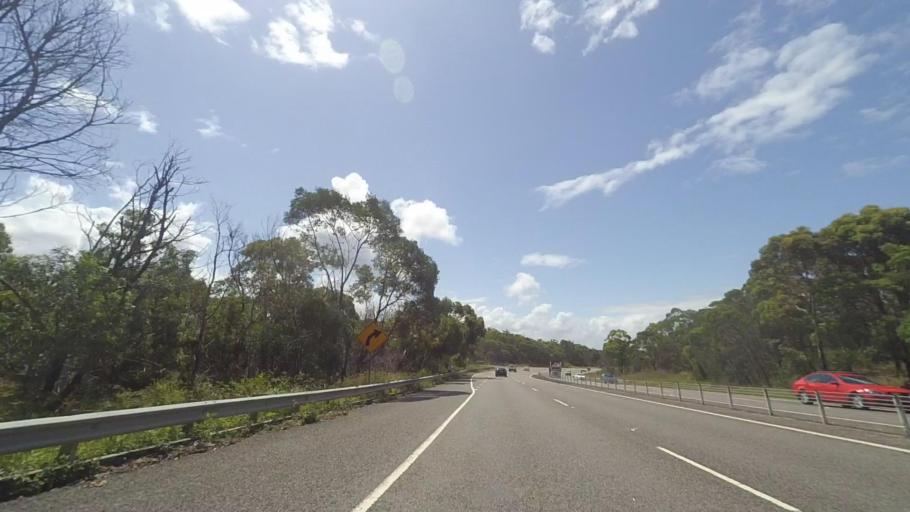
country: AU
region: New South Wales
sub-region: Wyong Shire
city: Kingfisher Shores
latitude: -33.1445
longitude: 151.6114
